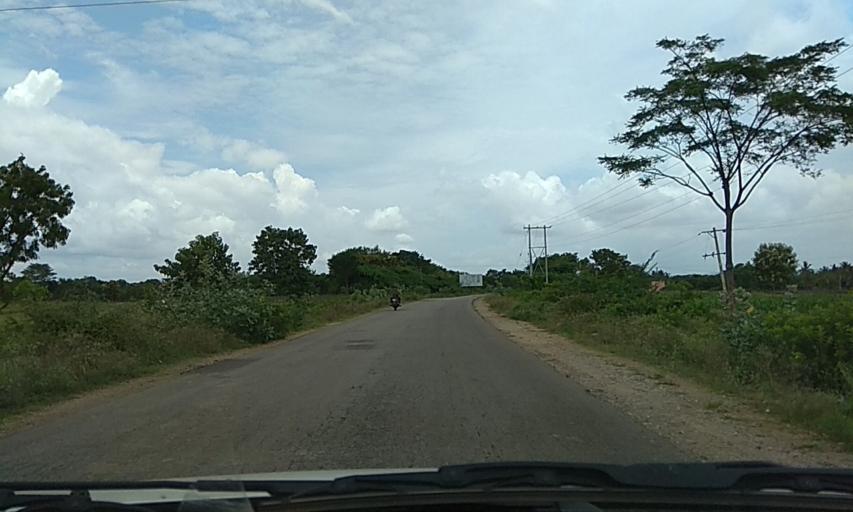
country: IN
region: Karnataka
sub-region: Chamrajnagar
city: Gundlupet
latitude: 11.8112
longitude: 76.7420
